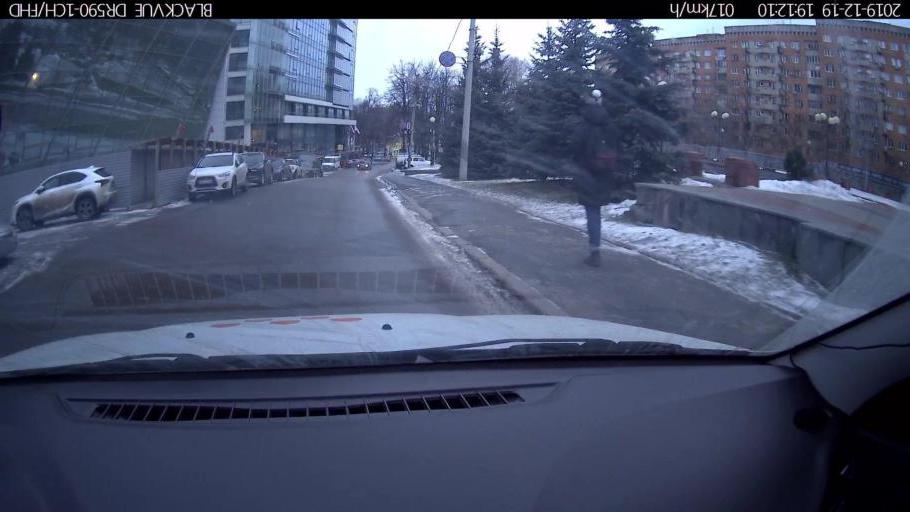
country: RU
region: Nizjnij Novgorod
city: Nizhniy Novgorod
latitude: 56.3165
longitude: 44.0023
